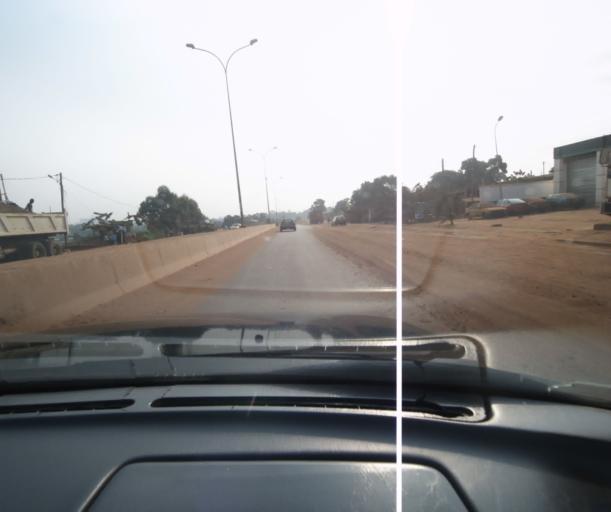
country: CM
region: Centre
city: Okoa
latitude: 3.9565
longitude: 11.5335
